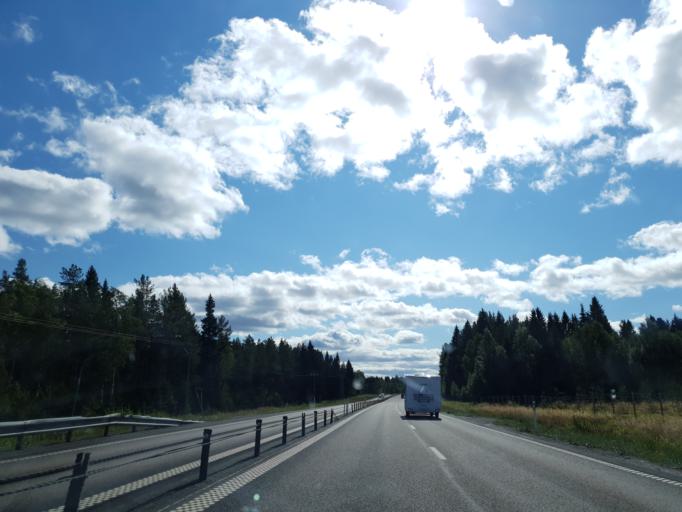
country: SE
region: Vaesternorrland
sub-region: OErnskoeldsviks Kommun
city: Husum
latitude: 63.4134
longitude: 19.2059
